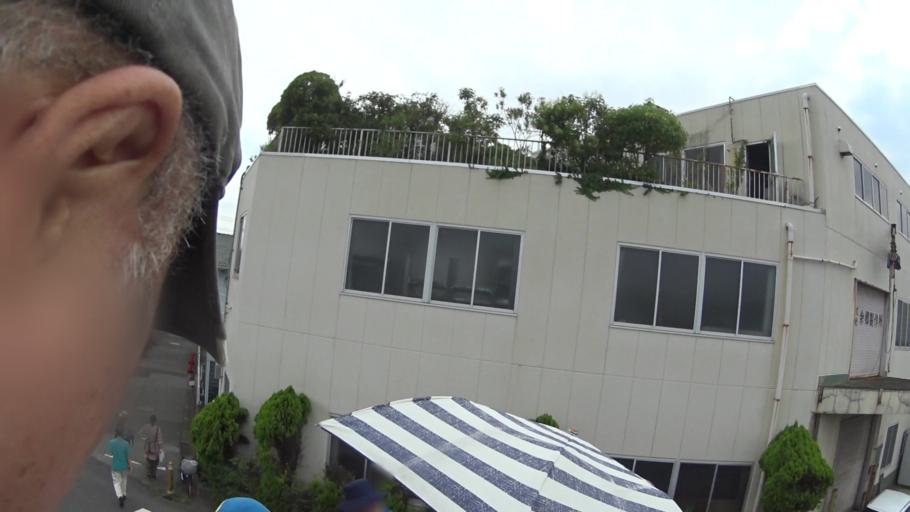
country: JP
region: Tokyo
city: Urayasu
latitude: 35.7057
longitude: 139.8512
